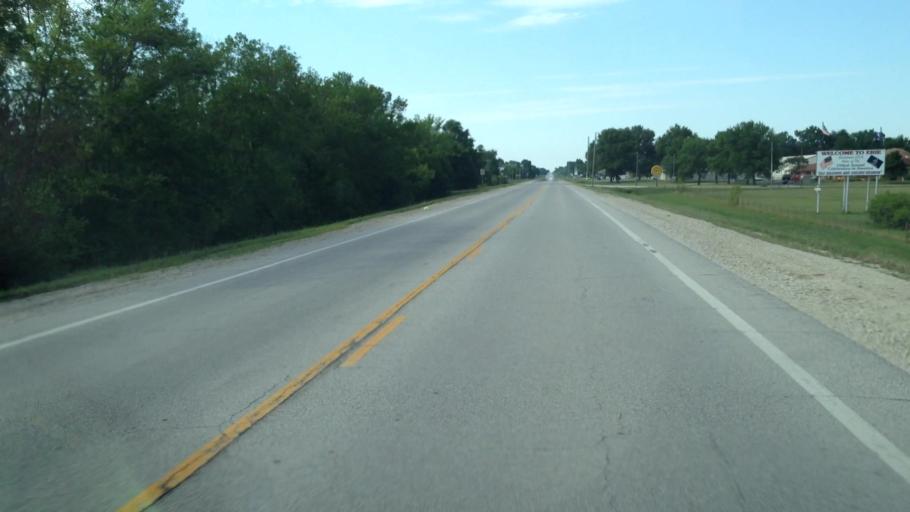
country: US
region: Kansas
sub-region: Neosho County
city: Erie
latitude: 37.5669
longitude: -95.2526
